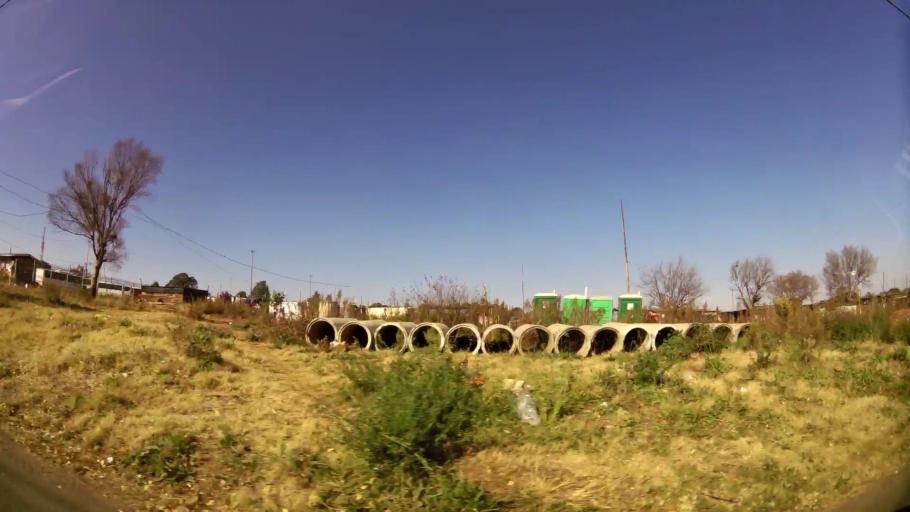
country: ZA
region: Gauteng
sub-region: City of Johannesburg Metropolitan Municipality
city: Johannesburg
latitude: -26.1925
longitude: 27.9781
